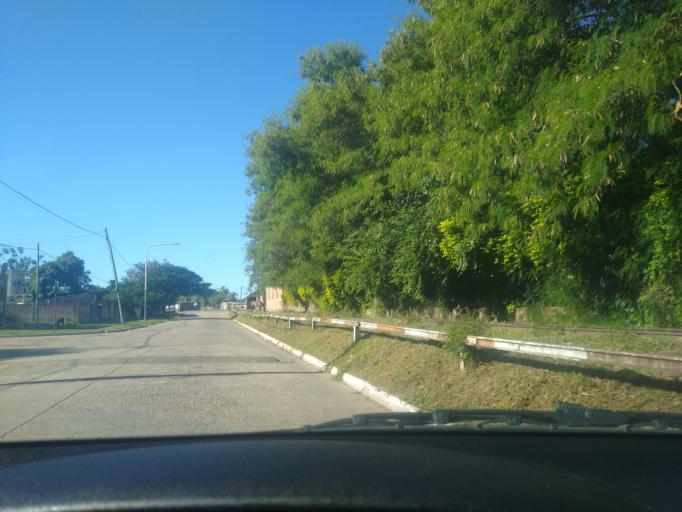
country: AR
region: Chaco
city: Puerto Vilelas
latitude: -27.5102
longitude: -58.9381
